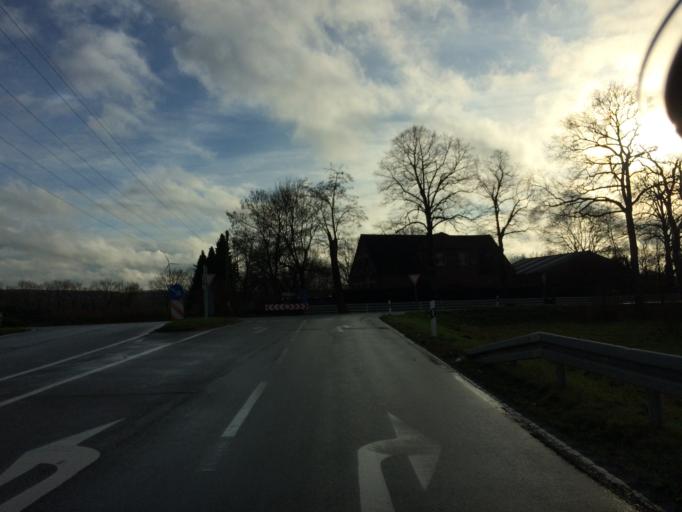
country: DE
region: North Rhine-Westphalia
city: Marl
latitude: 51.7000
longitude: 7.1302
